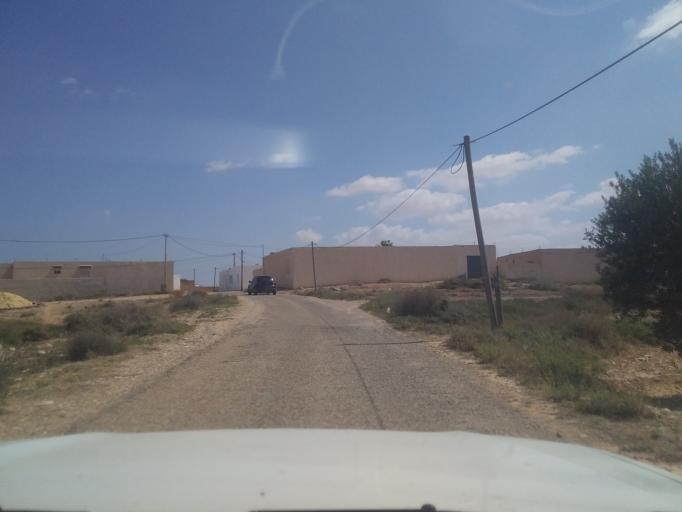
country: TN
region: Madanin
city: Medenine
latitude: 33.6104
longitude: 10.3101
